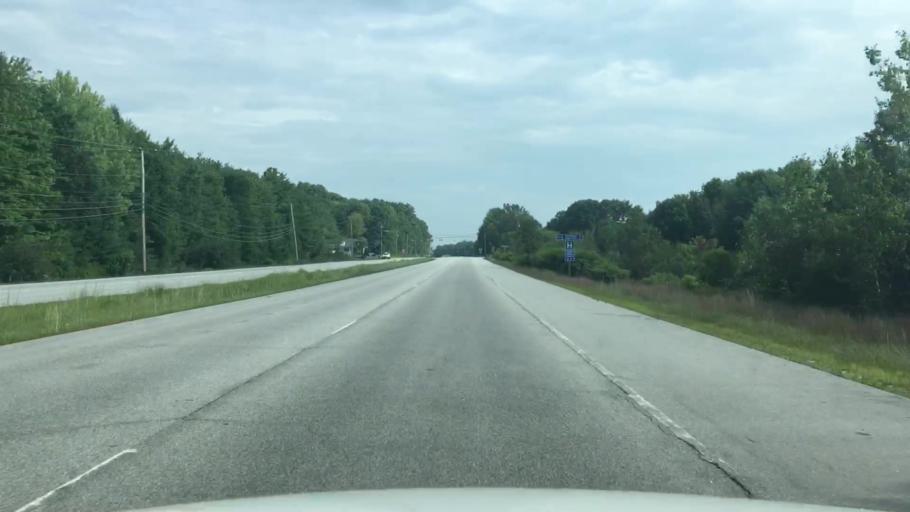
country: US
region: Maine
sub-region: Androscoggin County
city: Auburn
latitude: 44.0406
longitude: -70.2617
